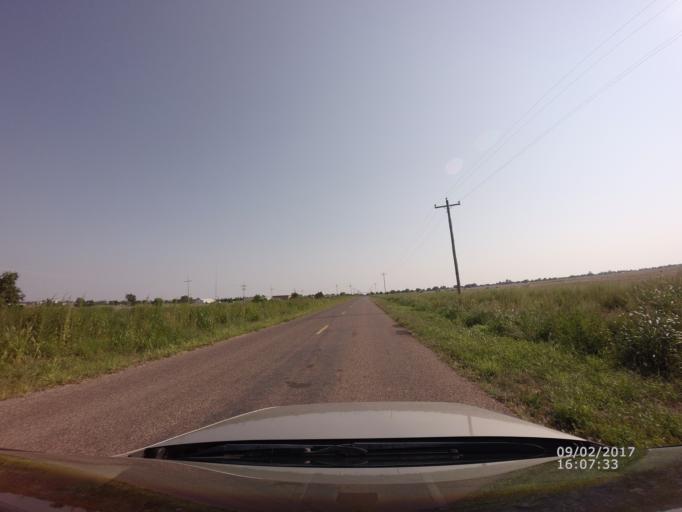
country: US
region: New Mexico
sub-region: Curry County
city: Clovis
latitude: 34.4382
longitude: -103.2141
